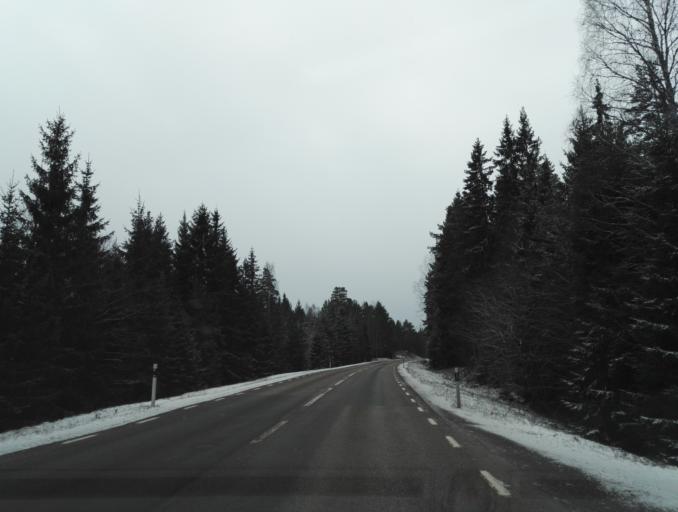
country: SE
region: Kalmar
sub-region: Hultsfreds Kommun
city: Virserum
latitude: 57.2744
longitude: 15.5706
